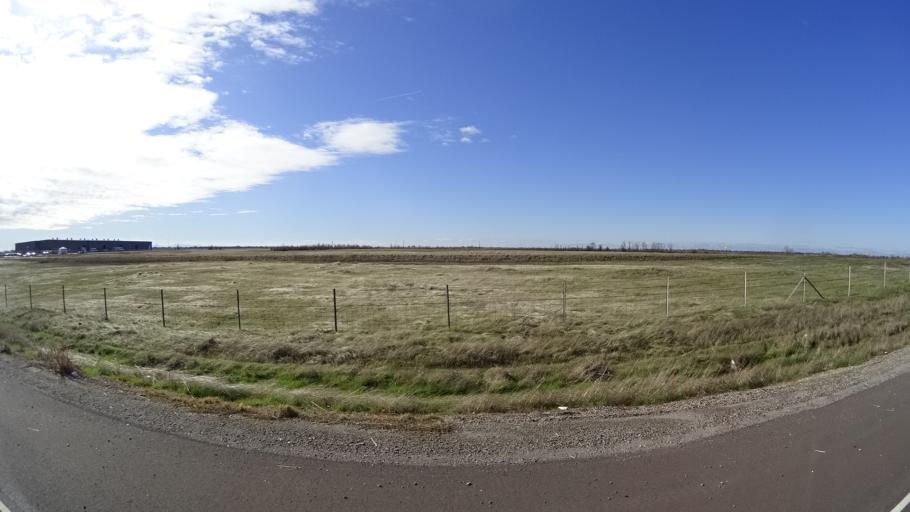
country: US
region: California
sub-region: Butte County
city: Durham
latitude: 39.6441
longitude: -121.7229
